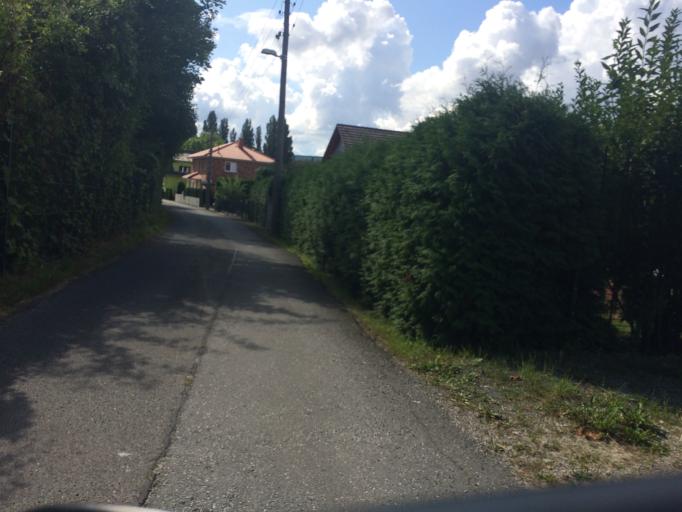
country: DE
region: Berlin
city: Heinersdorf
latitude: 52.5652
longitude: 13.4525
